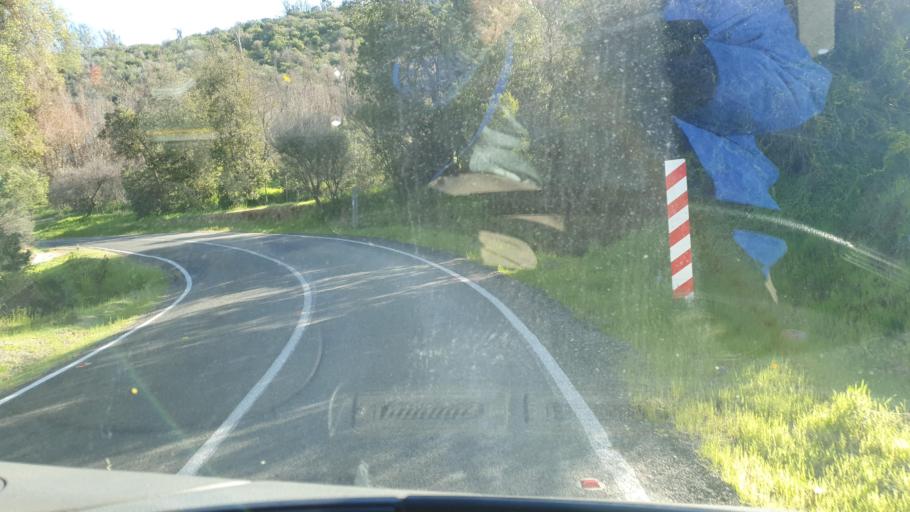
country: CL
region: Valparaiso
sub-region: Provincia de Marga Marga
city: Limache
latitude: -33.1794
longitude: -71.1739
